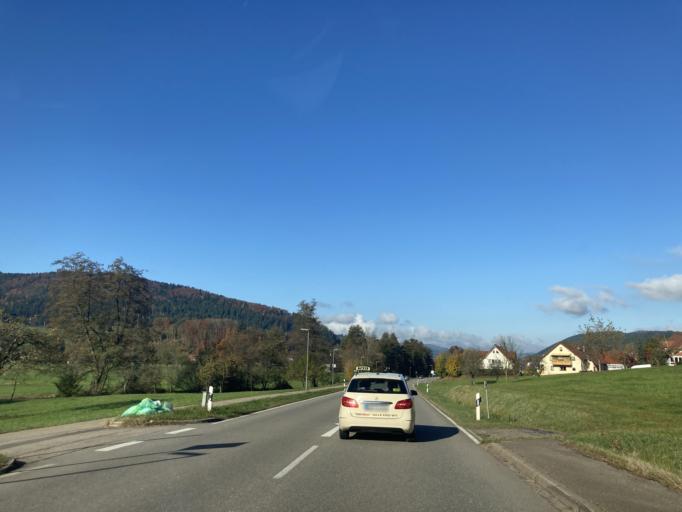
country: DE
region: Baden-Wuerttemberg
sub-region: Freiburg Region
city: Muhlenbach
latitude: 48.2682
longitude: 8.0959
